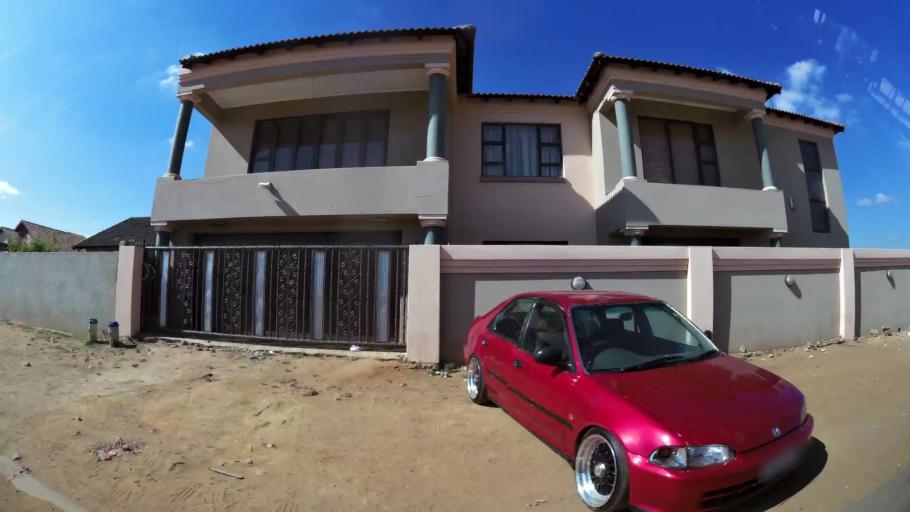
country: ZA
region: Gauteng
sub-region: West Rand District Municipality
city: Krugersdorp
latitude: -26.1486
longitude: 27.7724
